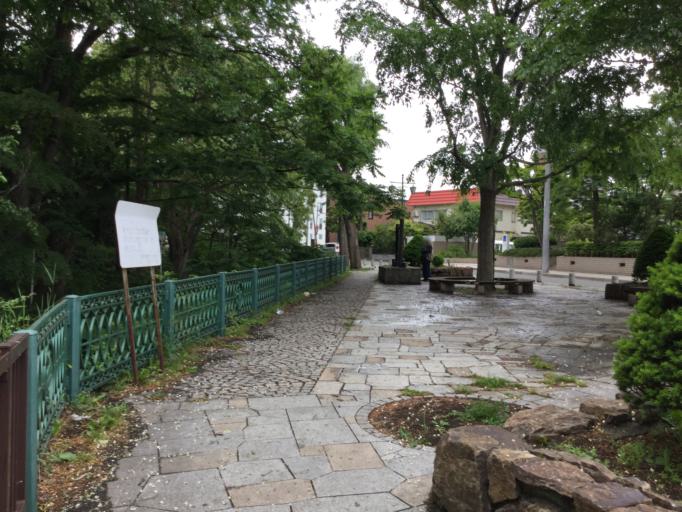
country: JP
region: Hokkaido
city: Sapporo
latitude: 43.0473
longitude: 141.3531
